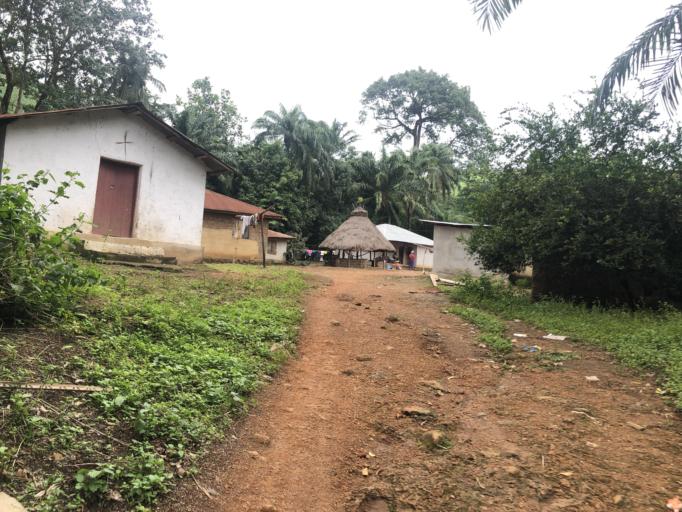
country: SL
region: Northern Province
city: Bumbuna
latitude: 8.9927
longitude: -11.7536
